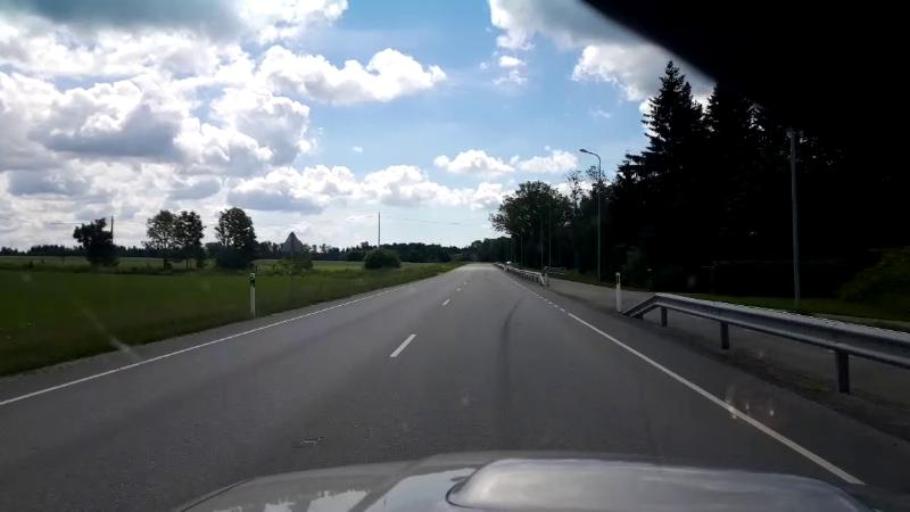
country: EE
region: Jaervamaa
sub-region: Jaerva-Jaani vald
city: Jarva-Jaani
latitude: 59.0258
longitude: 25.7043
